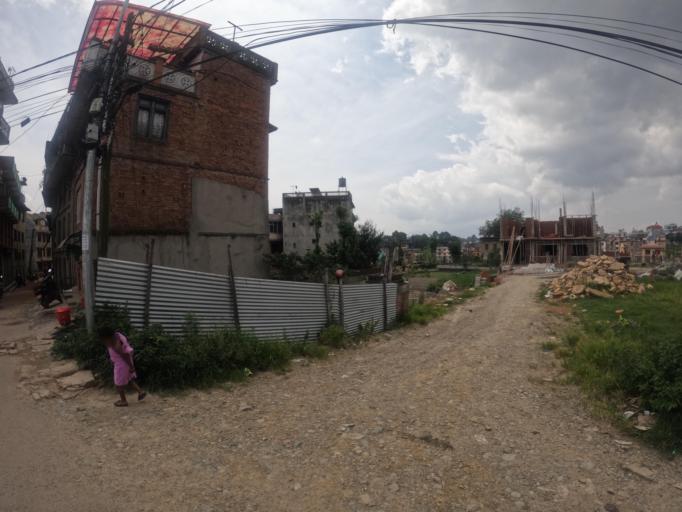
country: NP
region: Central Region
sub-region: Bagmati Zone
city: Bhaktapur
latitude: 27.6868
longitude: 85.3857
